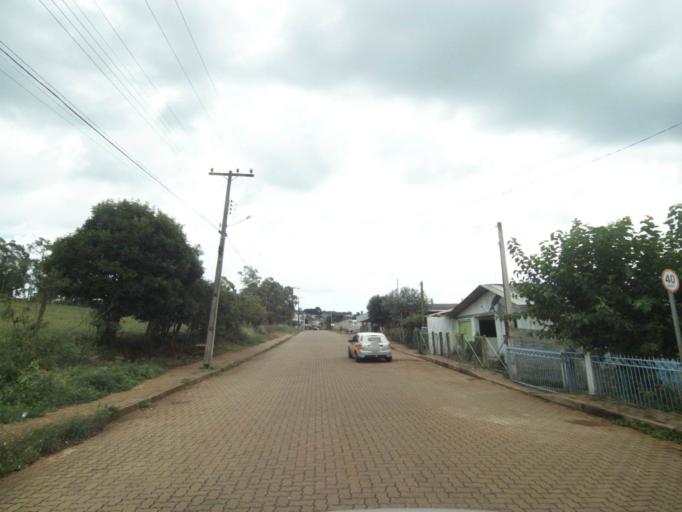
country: BR
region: Rio Grande do Sul
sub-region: Lagoa Vermelha
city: Lagoa Vermelha
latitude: -28.2283
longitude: -51.5163
